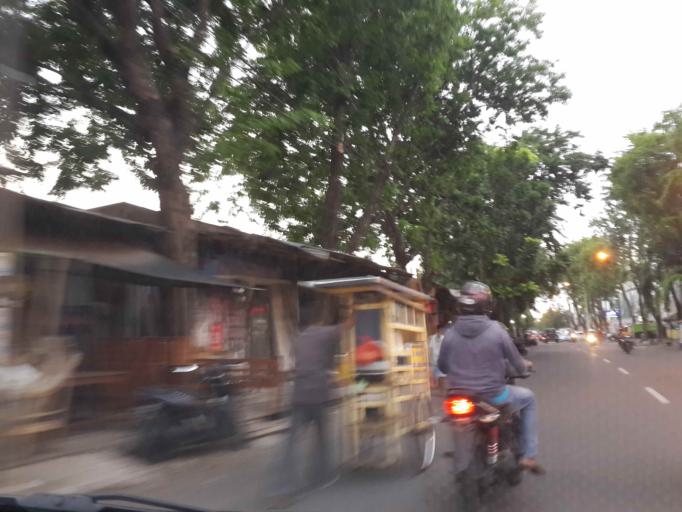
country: ID
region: East Java
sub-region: Kota Surabaya
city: Surabaya
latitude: -7.2506
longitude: 112.7299
